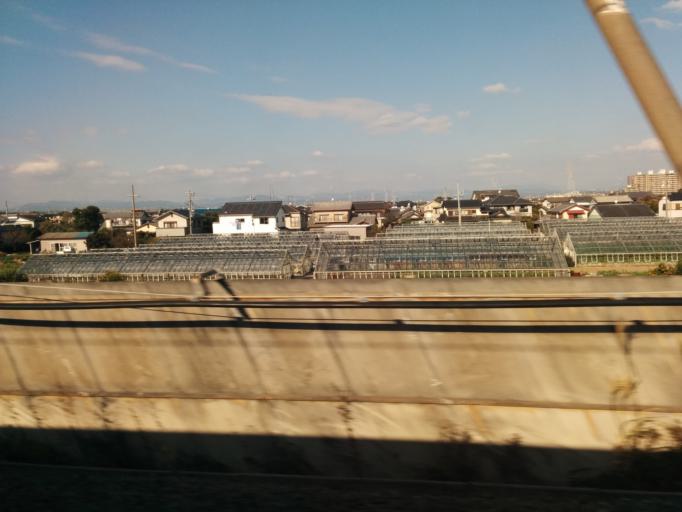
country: JP
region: Shizuoka
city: Iwata
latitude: 34.7028
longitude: 137.8174
